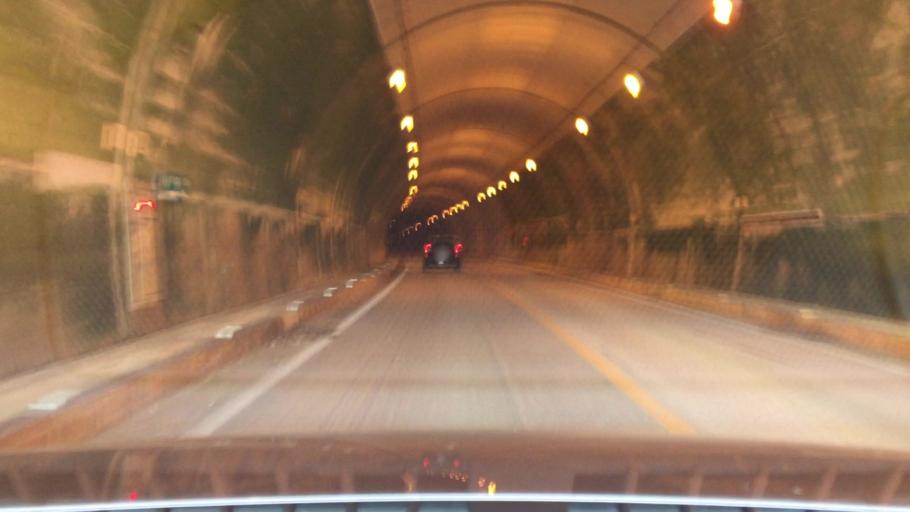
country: JP
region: Okinawa
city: Ishigaki
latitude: 24.4379
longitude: 124.2123
